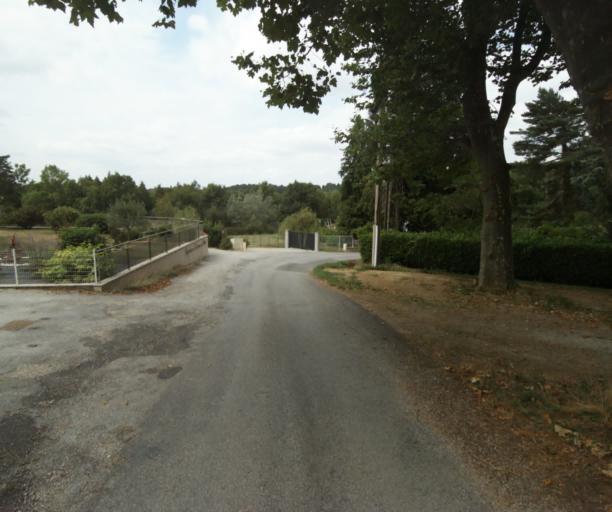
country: FR
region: Midi-Pyrenees
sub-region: Departement du Tarn
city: Soreze
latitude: 43.4324
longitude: 2.0371
